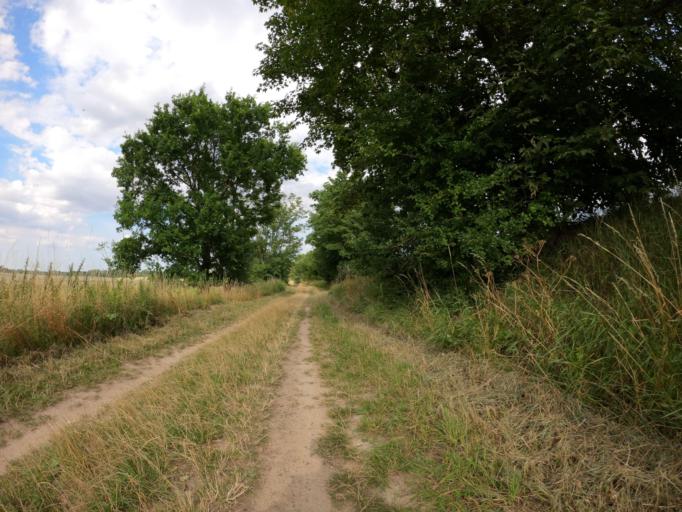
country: DE
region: Mecklenburg-Vorpommern
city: Woldegk
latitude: 53.4005
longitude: 13.6135
